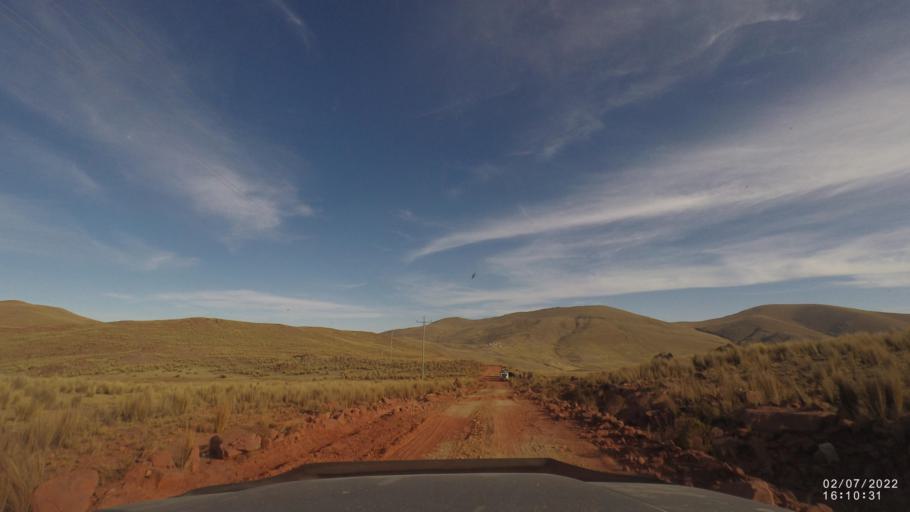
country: BO
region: Cochabamba
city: Irpa Irpa
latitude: -17.9130
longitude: -66.4400
